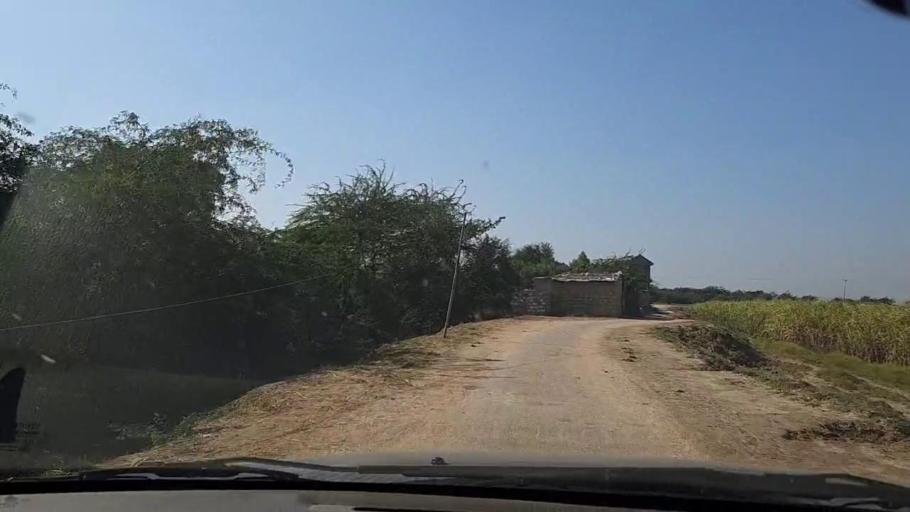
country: PK
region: Sindh
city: Thatta
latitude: 24.6032
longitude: 68.0529
